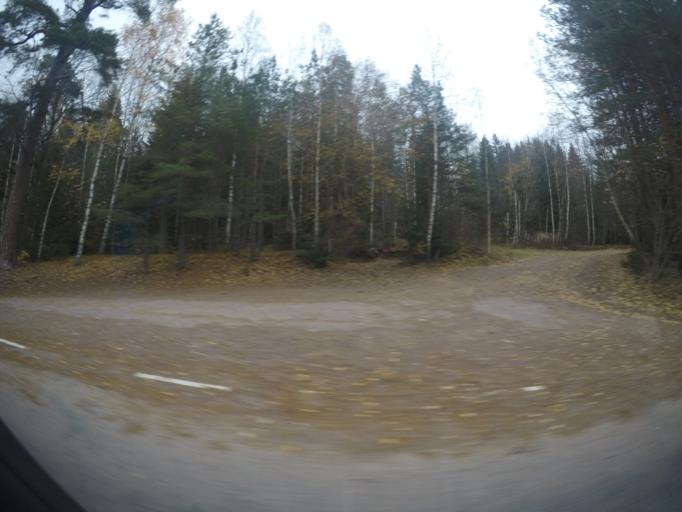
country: SE
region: Vaestmanland
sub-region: Surahammars Kommun
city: Surahammar
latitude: 59.6835
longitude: 16.0862
